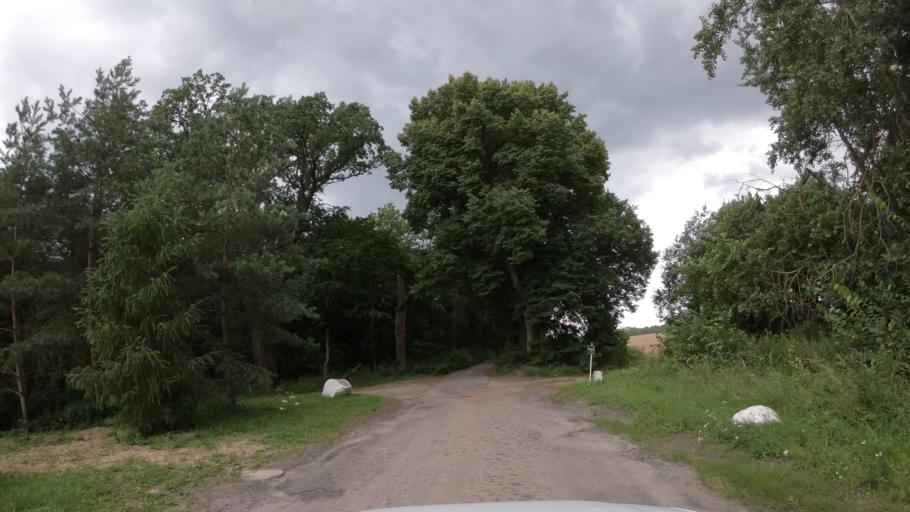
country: PL
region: West Pomeranian Voivodeship
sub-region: Powiat stargardzki
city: Dolice
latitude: 53.1898
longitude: 15.2959
